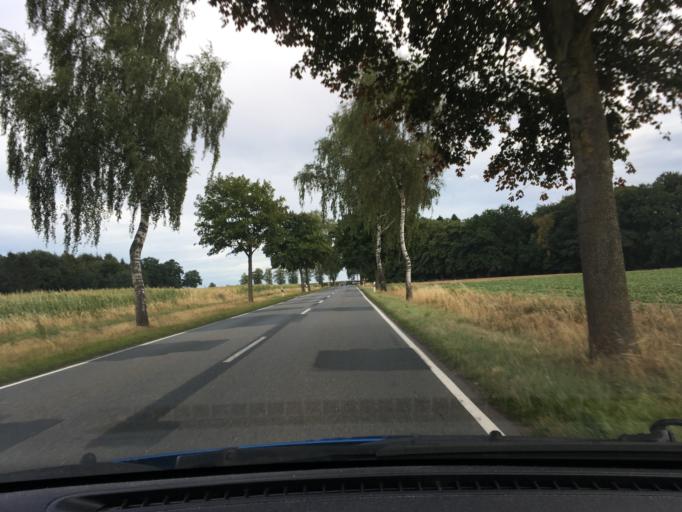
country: DE
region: Lower Saxony
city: Egestorf
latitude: 53.2021
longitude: 10.0483
